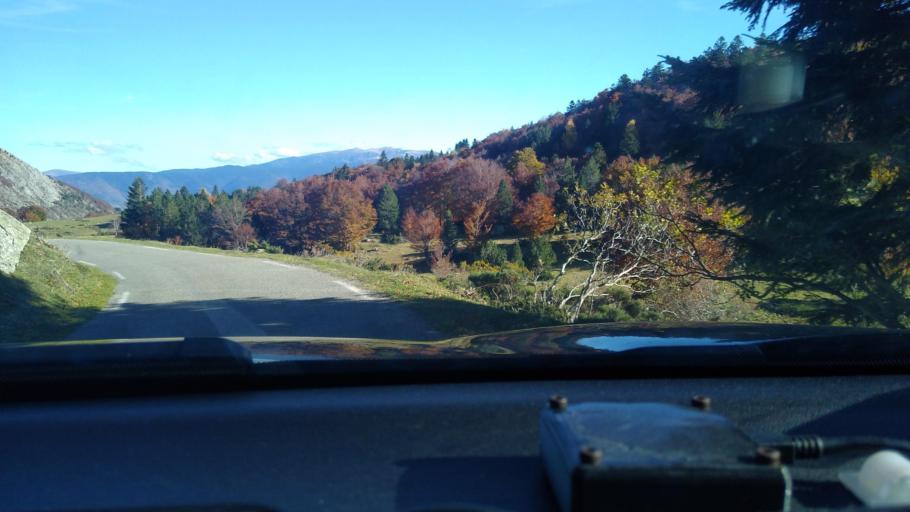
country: FR
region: Midi-Pyrenees
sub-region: Departement de l'Ariege
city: Ax-les-Thermes
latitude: 42.7286
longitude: 2.0061
